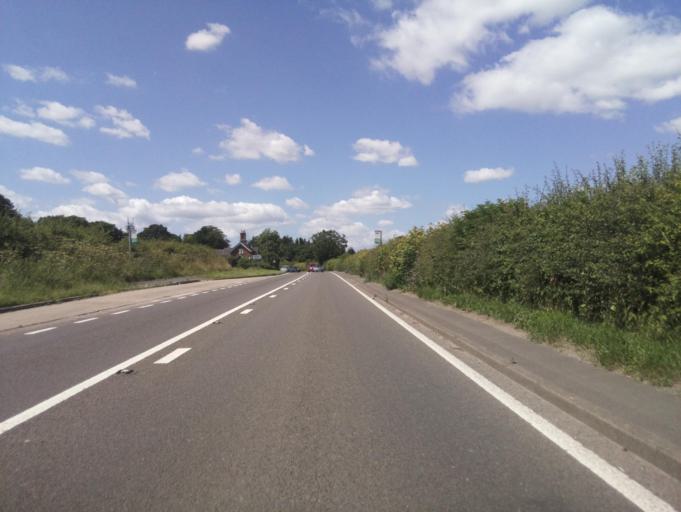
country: GB
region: England
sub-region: Derbyshire
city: Yeldersley
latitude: 52.9840
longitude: -1.6706
